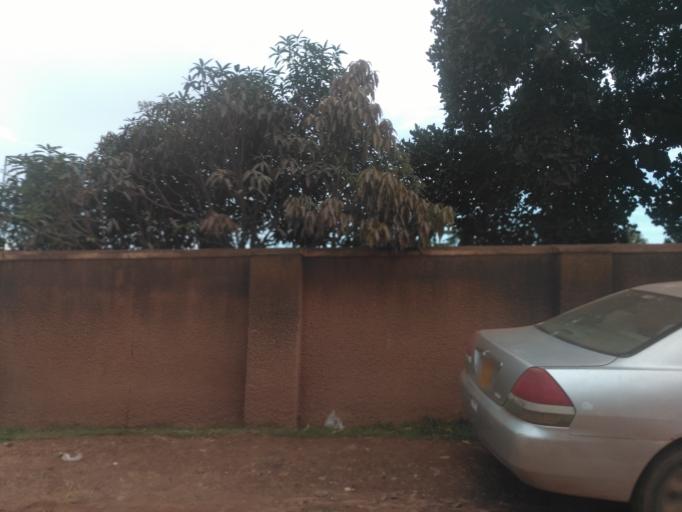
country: UG
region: Central Region
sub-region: Wakiso District
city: Kireka
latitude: 0.3744
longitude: 32.6152
